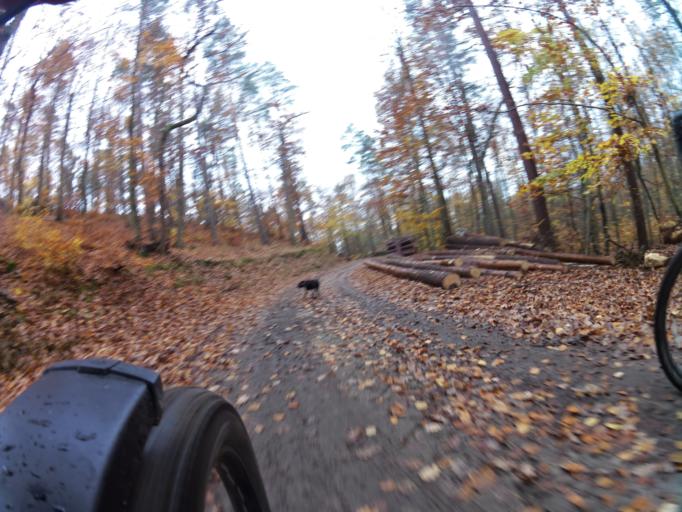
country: PL
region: Pomeranian Voivodeship
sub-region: Powiat pucki
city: Krokowa
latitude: 54.7479
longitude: 18.0918
